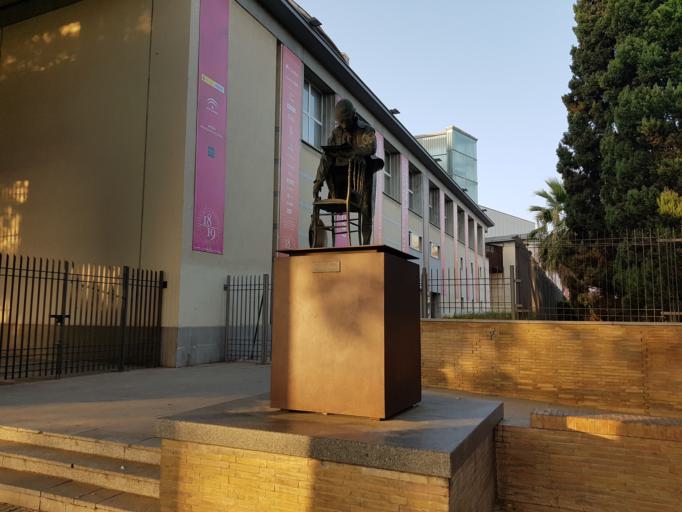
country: ES
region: Andalusia
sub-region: Provincia de Sevilla
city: Sevilla
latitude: 37.3836
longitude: -5.9968
